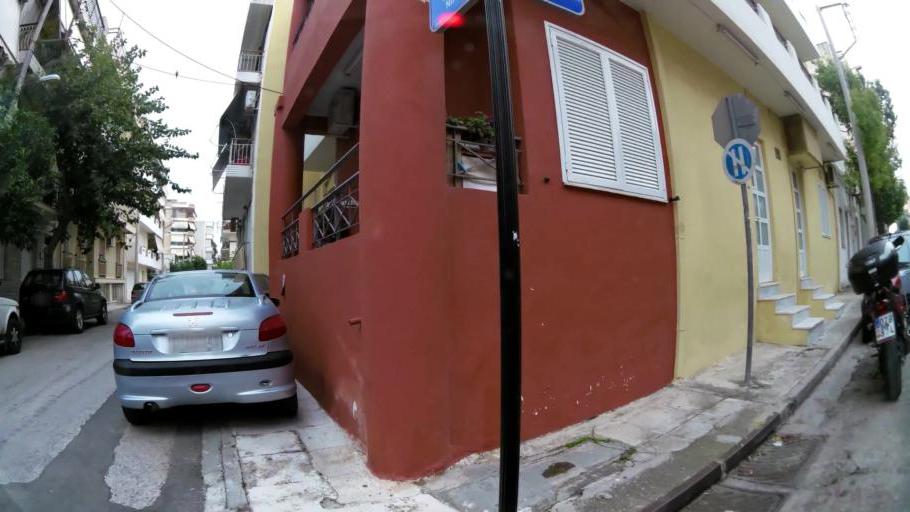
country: GR
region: Attica
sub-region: Nomarchia Athinas
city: Agioi Anargyroi
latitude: 38.0245
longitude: 23.7124
